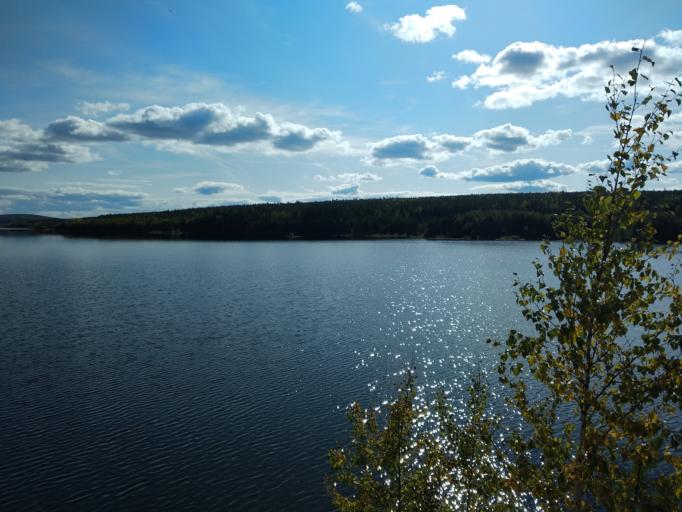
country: RU
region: Sverdlovsk
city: Karpinsk
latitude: 59.8104
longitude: 59.7939
